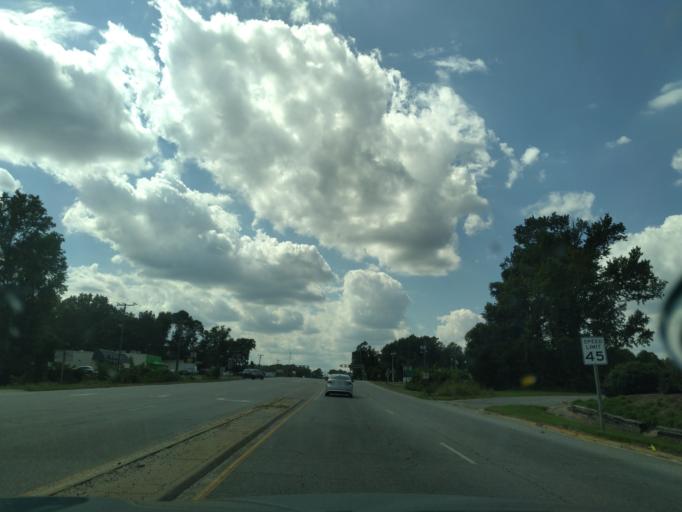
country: US
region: North Carolina
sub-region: Martin County
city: Williamston
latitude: 35.8437
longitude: -77.0561
